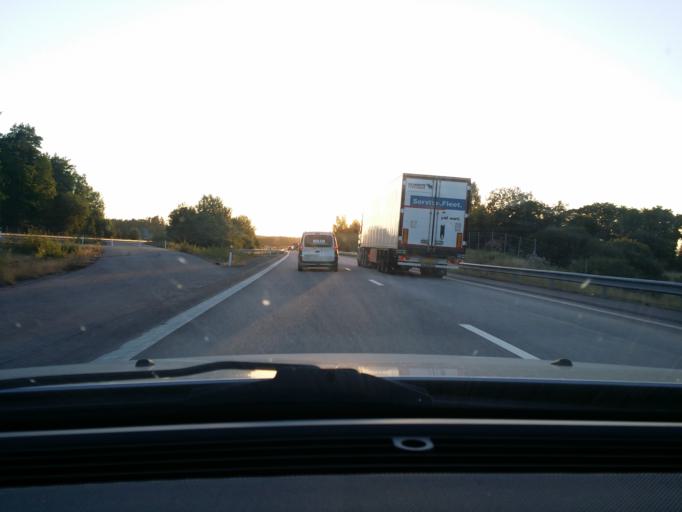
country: SE
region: Uppsala
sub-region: Enkopings Kommun
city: Grillby
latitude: 59.6388
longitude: 17.2605
